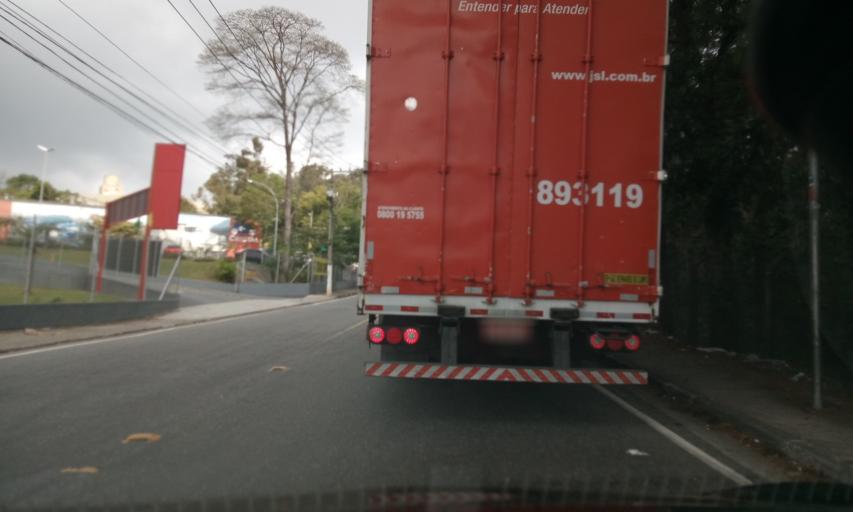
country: BR
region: Sao Paulo
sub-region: Sao Caetano Do Sul
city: Sao Caetano do Sul
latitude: -23.6489
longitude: -46.5844
